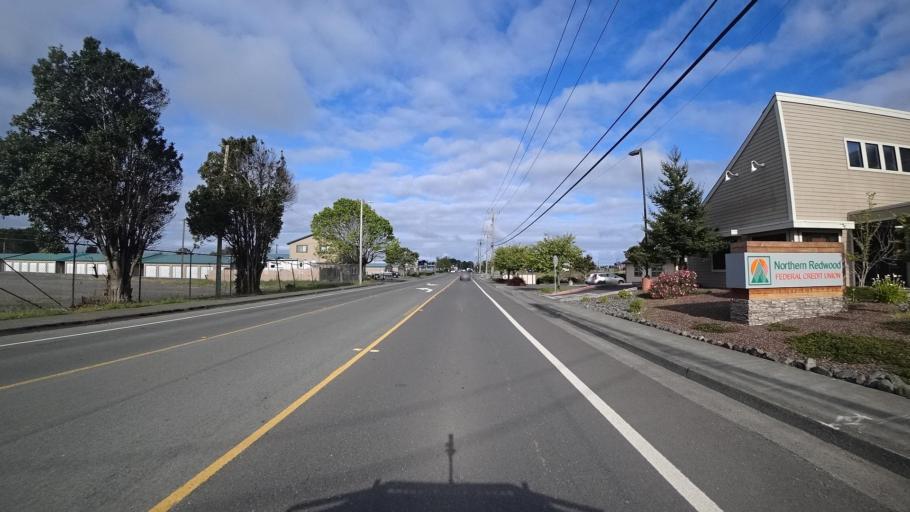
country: US
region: California
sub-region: Humboldt County
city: Arcata
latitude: 40.9050
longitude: -124.0782
